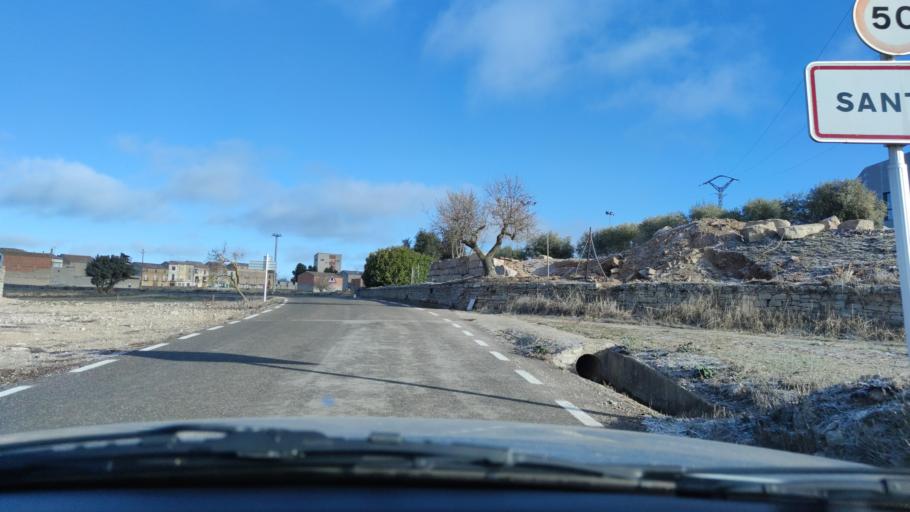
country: ES
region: Catalonia
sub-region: Provincia de Lleida
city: Ivorra
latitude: 41.7226
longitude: 1.3597
